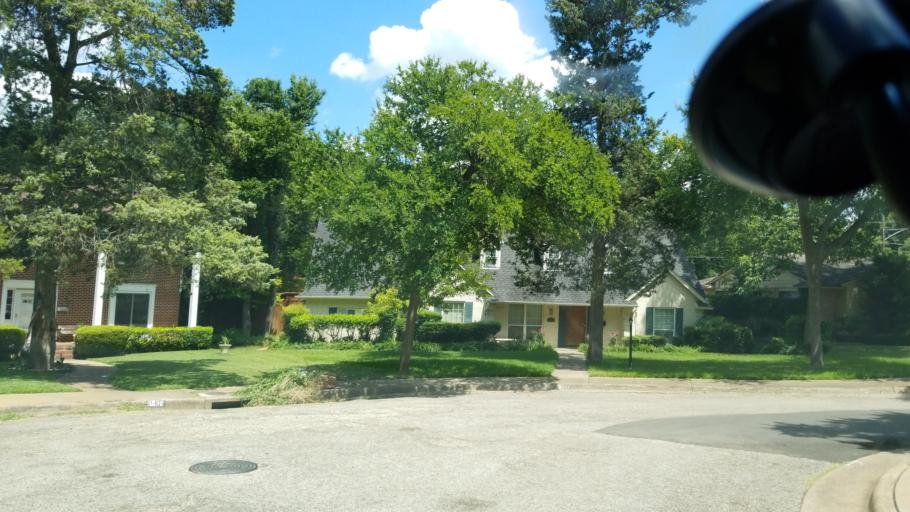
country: US
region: Texas
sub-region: Dallas County
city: Cockrell Hill
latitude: 32.6987
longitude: -96.8729
